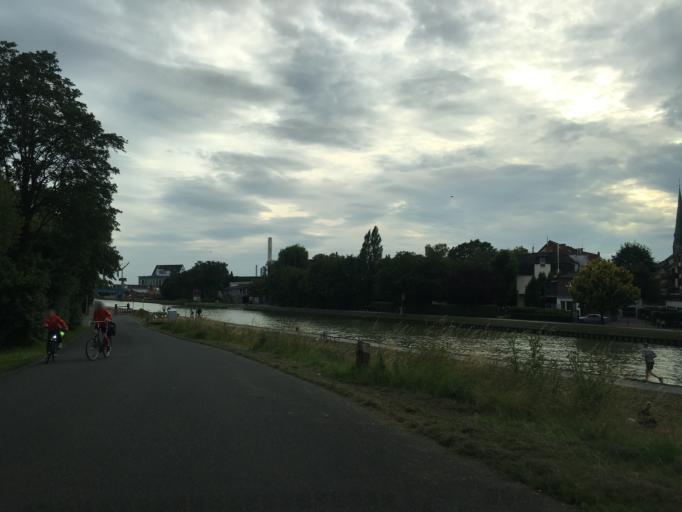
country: DE
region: North Rhine-Westphalia
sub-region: Regierungsbezirk Munster
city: Muenster
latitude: 51.9543
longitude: 7.6561
